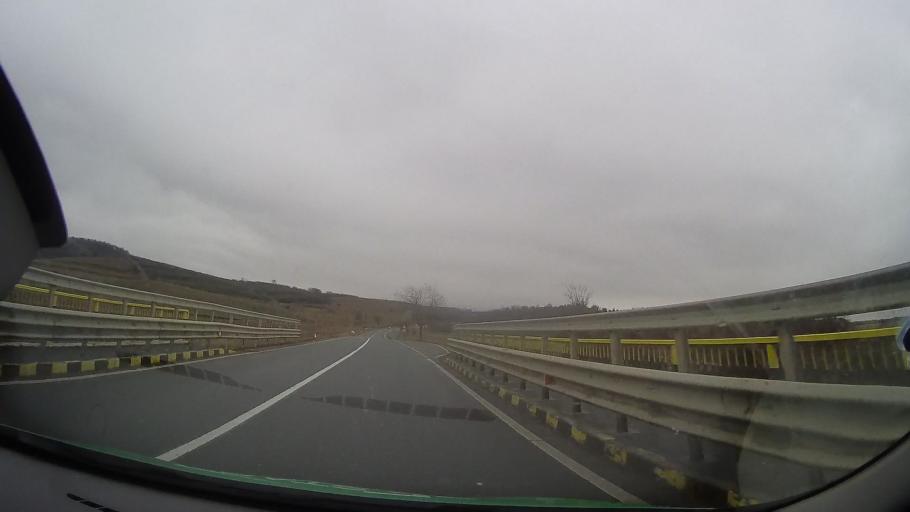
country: RO
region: Mures
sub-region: Comuna Breaza
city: Breaza
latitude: 46.7880
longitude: 24.6449
